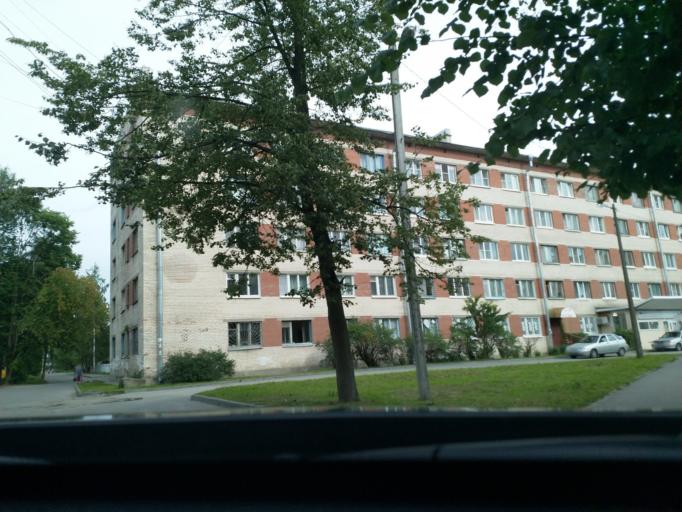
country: RU
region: Leningrad
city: Nikol'skoye
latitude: 59.7041
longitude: 30.7898
